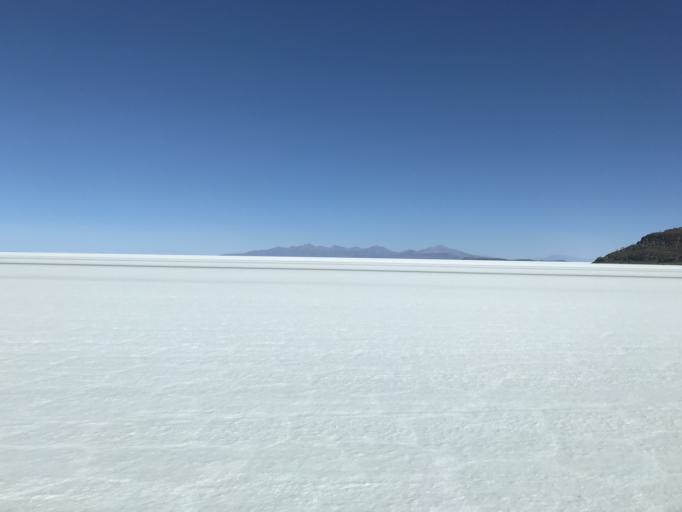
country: BO
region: Potosi
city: Colchani
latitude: -20.2383
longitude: -67.6195
